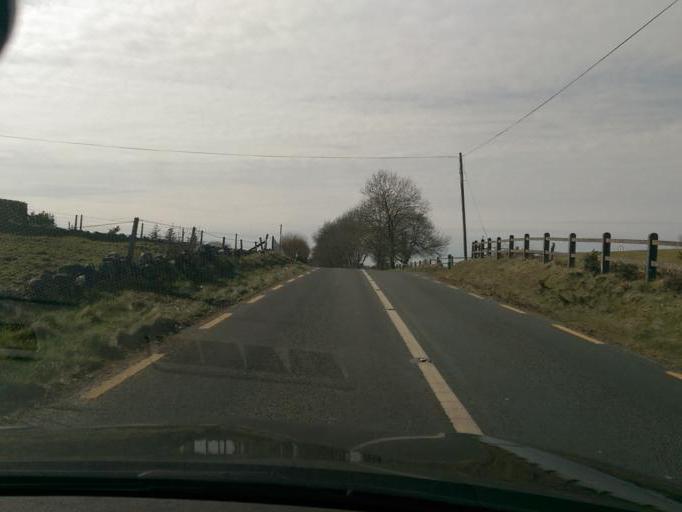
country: IE
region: Connaught
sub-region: County Galway
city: Athenry
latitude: 53.4781
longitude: -8.6123
